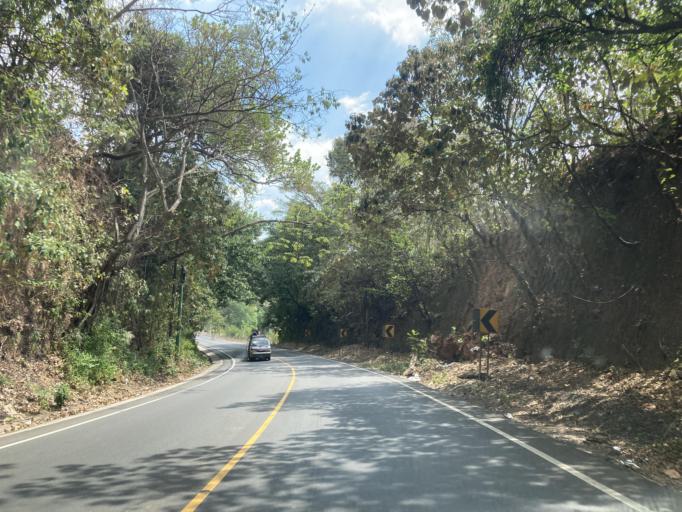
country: GT
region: Santa Rosa
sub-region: Municipio de Taxisco
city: Taxisco
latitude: 14.0758
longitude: -90.4798
